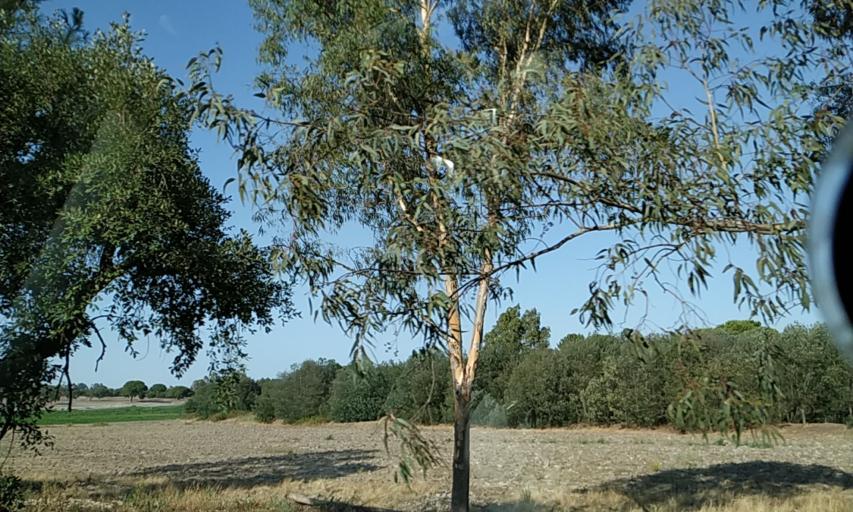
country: PT
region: Santarem
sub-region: Coruche
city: Coruche
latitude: 38.9926
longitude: -8.5542
